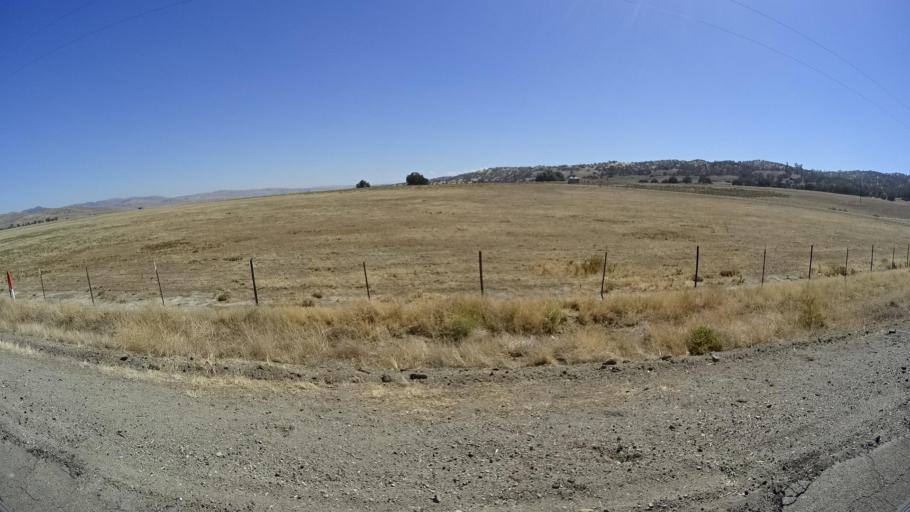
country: US
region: California
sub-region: San Luis Obispo County
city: Shandon
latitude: 35.8014
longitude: -120.3639
